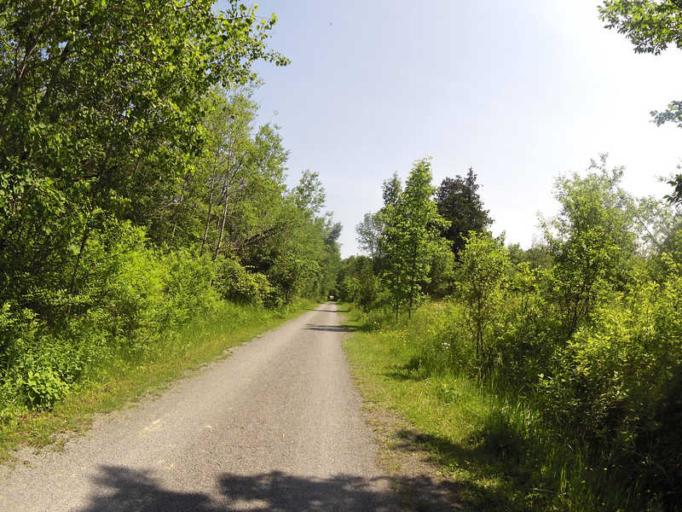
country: CA
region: Ontario
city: Peterborough
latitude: 44.3801
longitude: -78.2762
